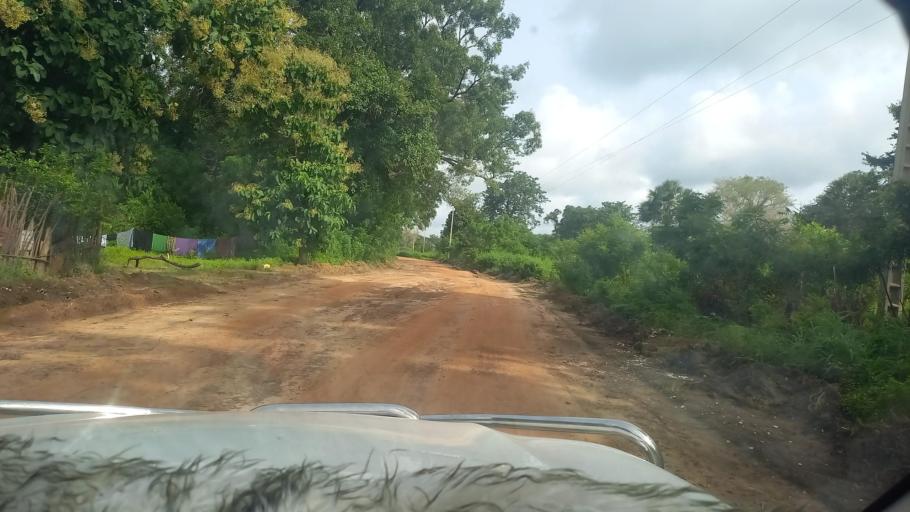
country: SN
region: Ziguinchor
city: Ziguinchor
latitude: 12.6659
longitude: -16.2655
